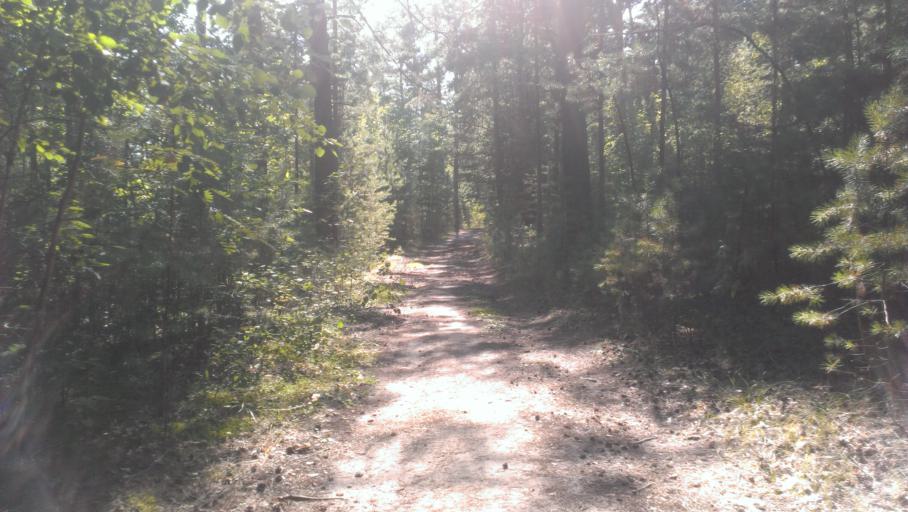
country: RU
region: Altai Krai
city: Yuzhnyy
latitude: 53.3155
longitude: 83.6884
